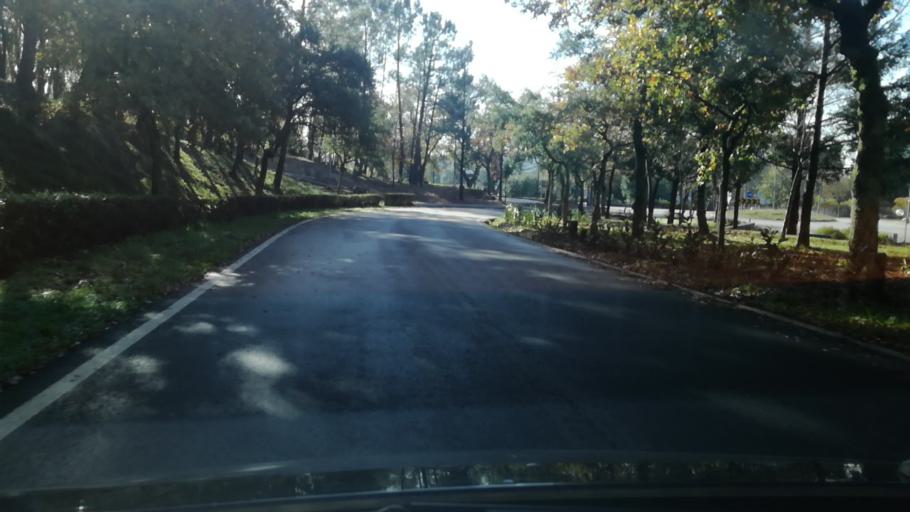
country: PT
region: Braga
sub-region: Braga
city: Braga
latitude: 41.5421
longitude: -8.3723
